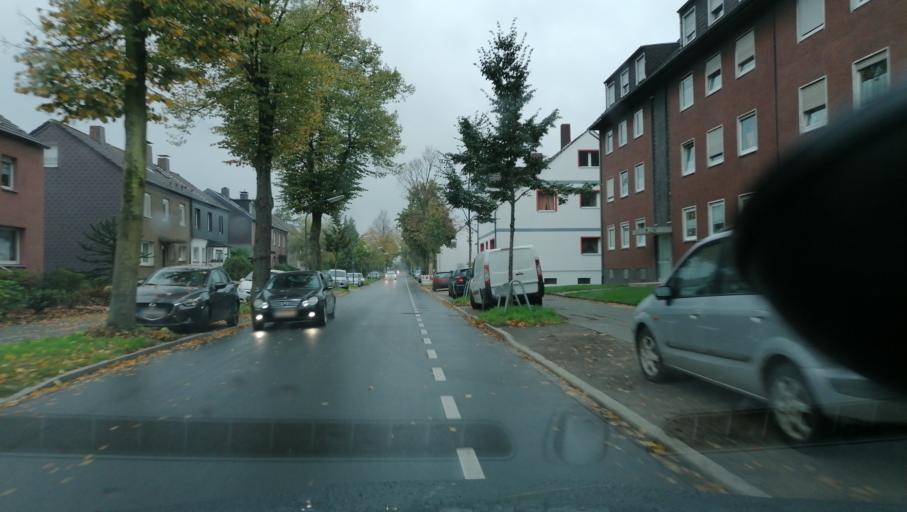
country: DE
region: North Rhine-Westphalia
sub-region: Regierungsbezirk Arnsberg
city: Herne
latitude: 51.5640
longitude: 7.2032
